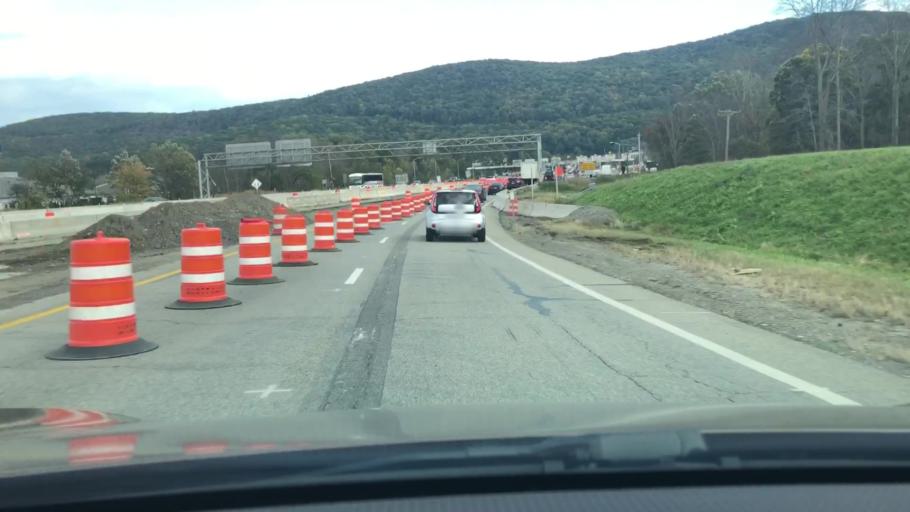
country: US
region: New York
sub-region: Orange County
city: Harriman
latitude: 41.3152
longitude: -74.1317
